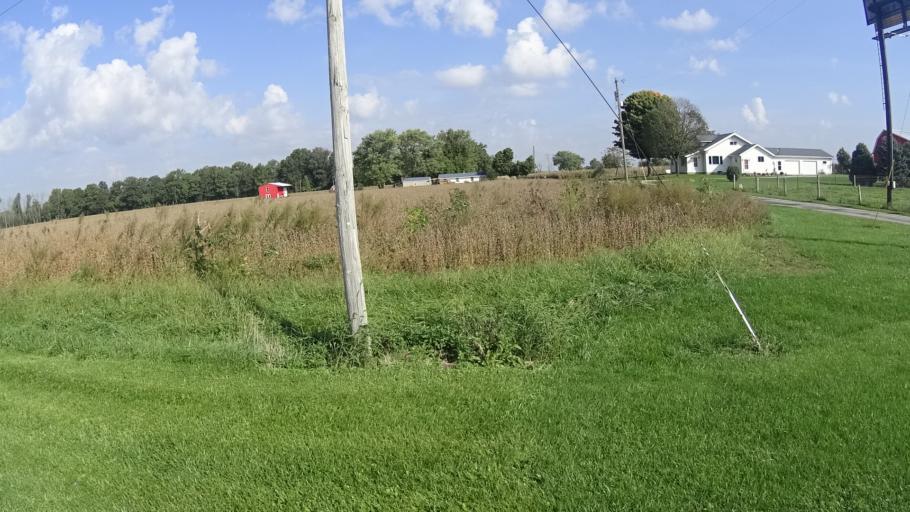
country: US
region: Indiana
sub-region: Madison County
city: Ingalls
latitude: 39.9917
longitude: -85.8245
